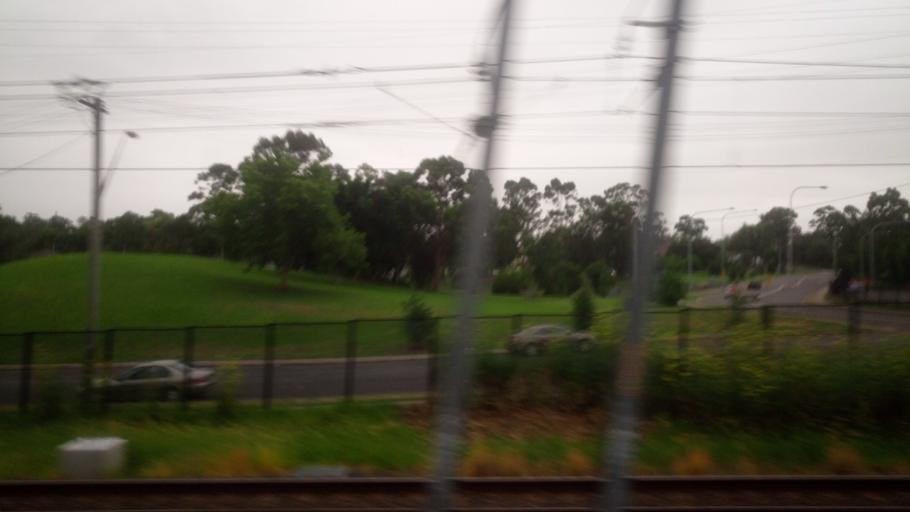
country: AU
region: New South Wales
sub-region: Blacktown
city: Blacktown
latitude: -33.7742
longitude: 150.9345
